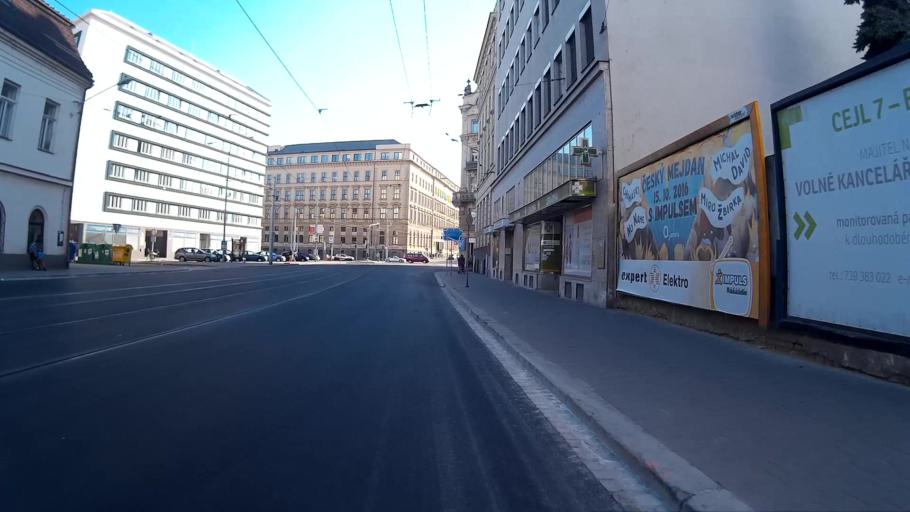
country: CZ
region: South Moravian
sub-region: Mesto Brno
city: Brno
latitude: 49.1967
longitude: 16.6167
